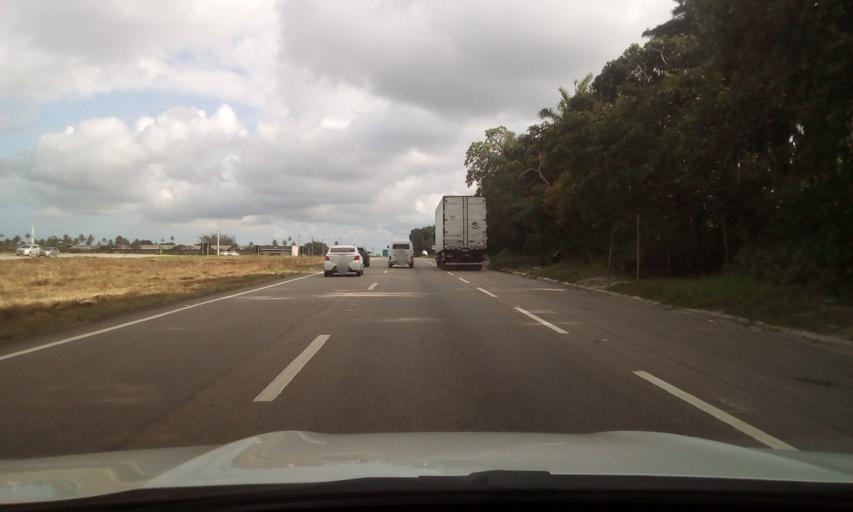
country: BR
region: Pernambuco
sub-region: Itapissuma
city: Itapissuma
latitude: -7.7945
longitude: -34.9283
